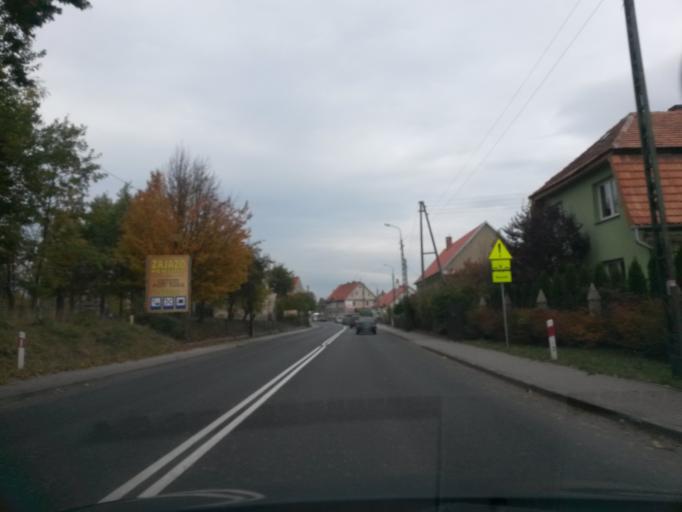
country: PL
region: Lower Silesian Voivodeship
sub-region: Powiat dzierzoniowski
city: Niemcza
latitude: 50.6836
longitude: 16.8202
